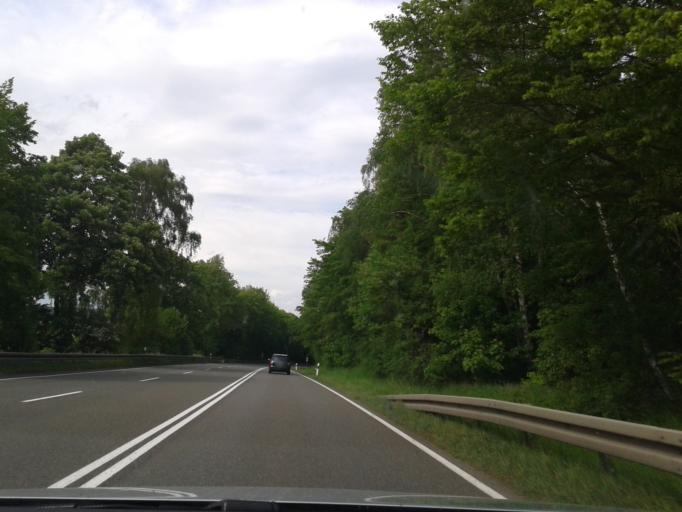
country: DE
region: Hesse
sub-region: Regierungsbezirk Kassel
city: Korbach
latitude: 51.2986
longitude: 8.8871
